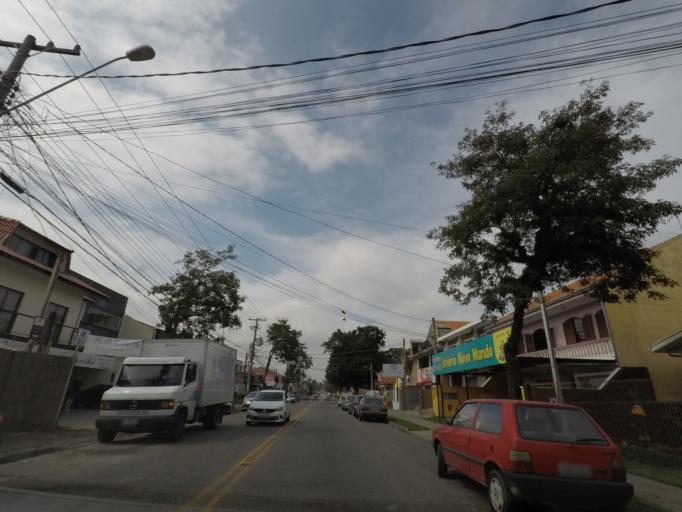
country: BR
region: Parana
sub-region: Curitiba
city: Curitiba
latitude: -25.4890
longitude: -49.3033
